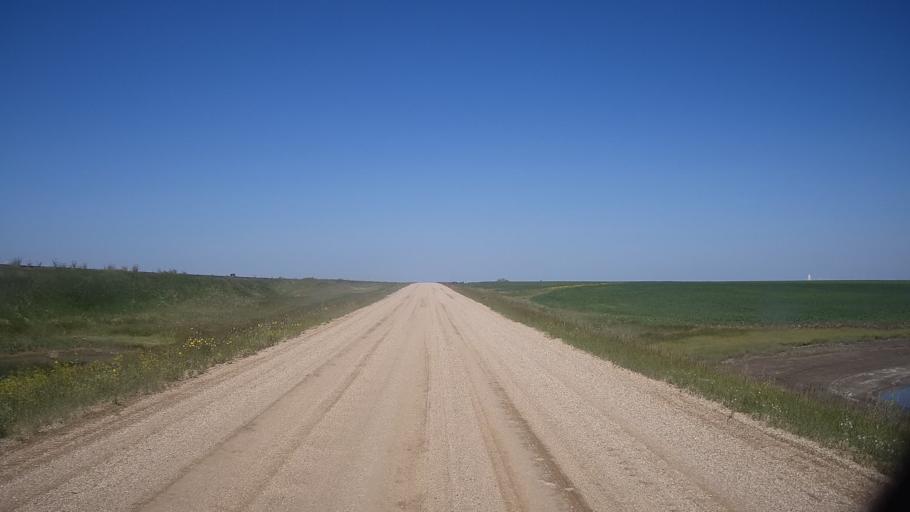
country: CA
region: Saskatchewan
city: Watrous
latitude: 51.8781
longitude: -106.0141
